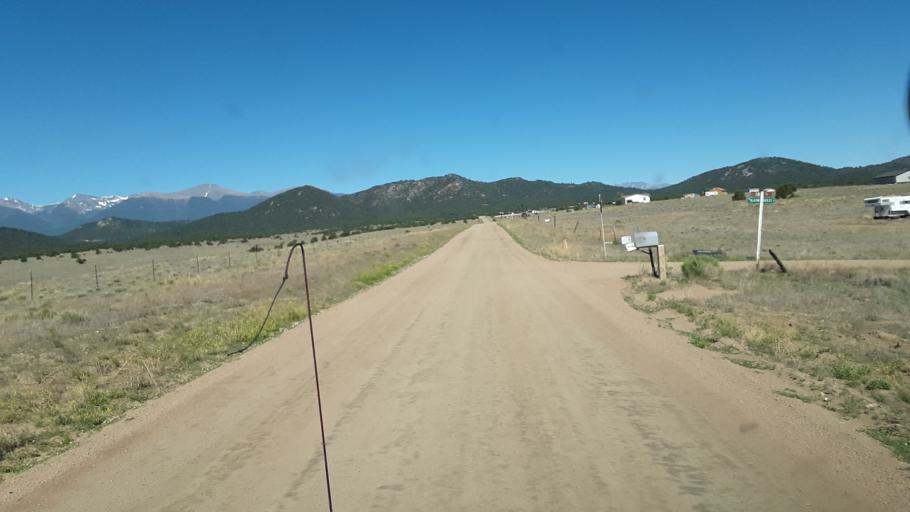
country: US
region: Colorado
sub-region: Custer County
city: Westcliffe
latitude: 38.2848
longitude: -105.5073
